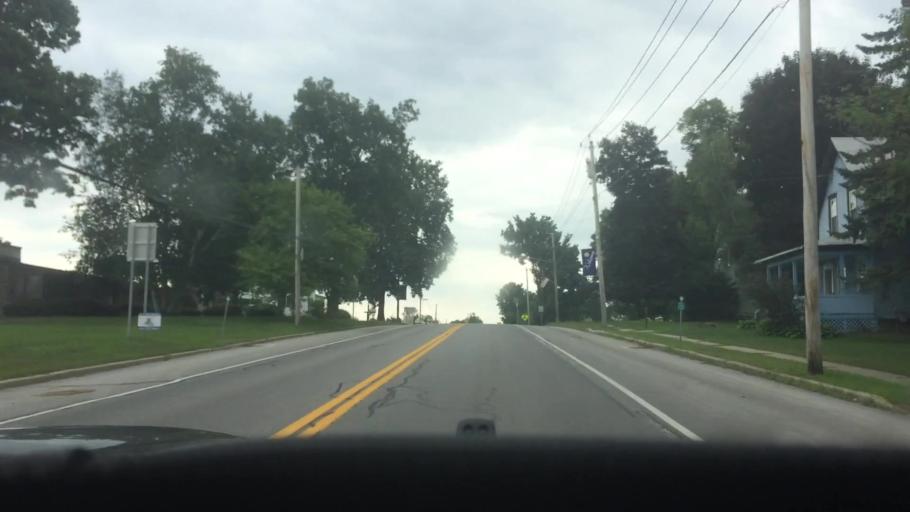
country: US
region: New York
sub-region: St. Lawrence County
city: Ogdensburg
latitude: 44.6138
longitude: -75.4014
